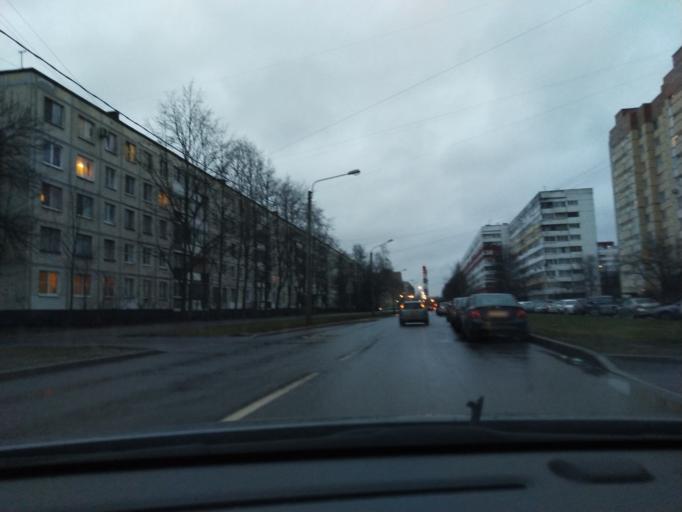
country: RU
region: St.-Petersburg
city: Uritsk
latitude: 59.8287
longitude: 30.1824
